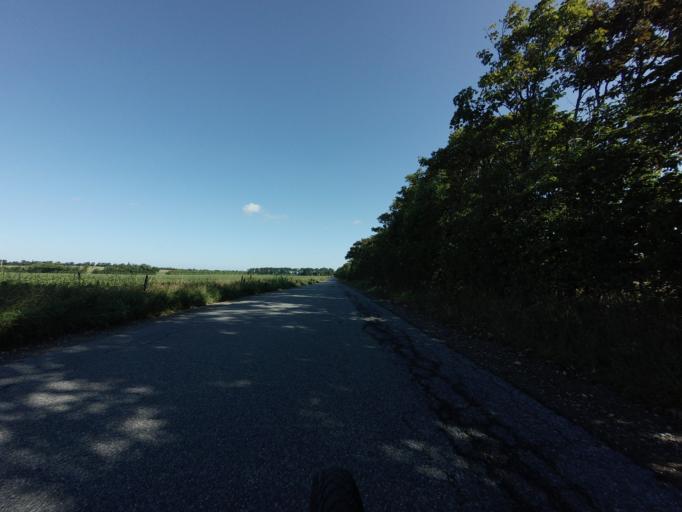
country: DK
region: North Denmark
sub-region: Hjorring Kommune
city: Vra
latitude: 57.3664
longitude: 10.0034
